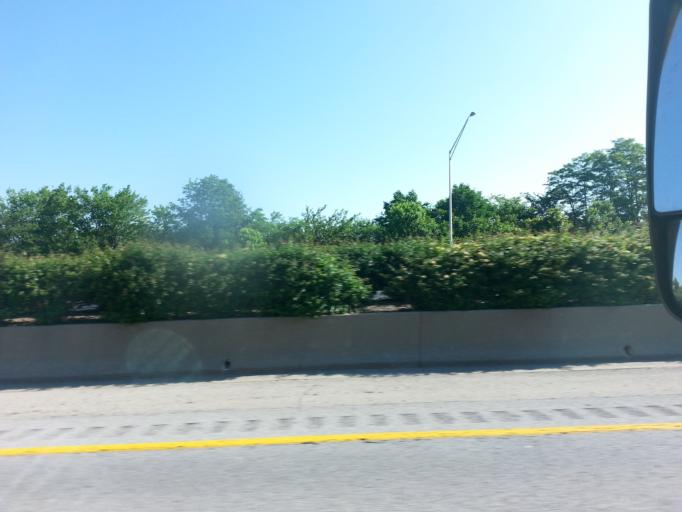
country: US
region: Kentucky
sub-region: Jefferson County
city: Hurstbourne Acres
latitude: 38.2247
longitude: -85.5832
